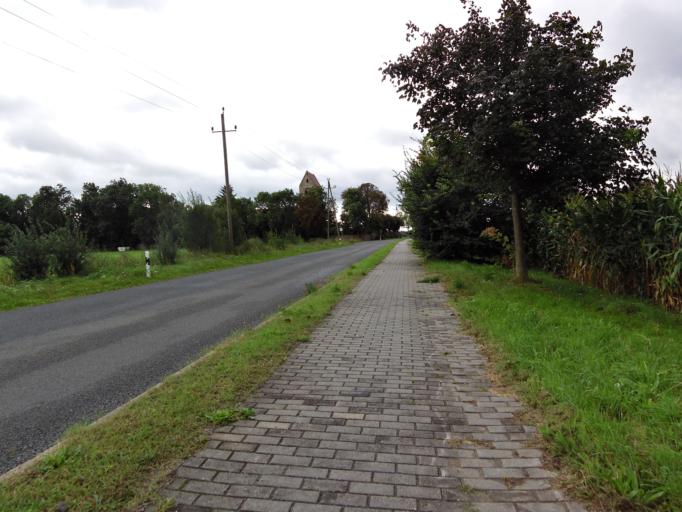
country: DE
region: Saxony-Anhalt
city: Hohenberg-Krusemark
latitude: 52.7147
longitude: 11.9514
